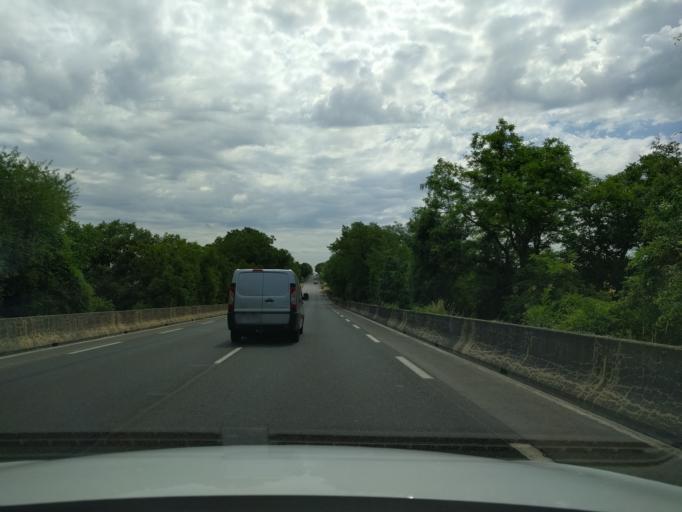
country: FR
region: Poitou-Charentes
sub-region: Departement des Deux-Sevres
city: Bessines
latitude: 46.3444
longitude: -0.4992
